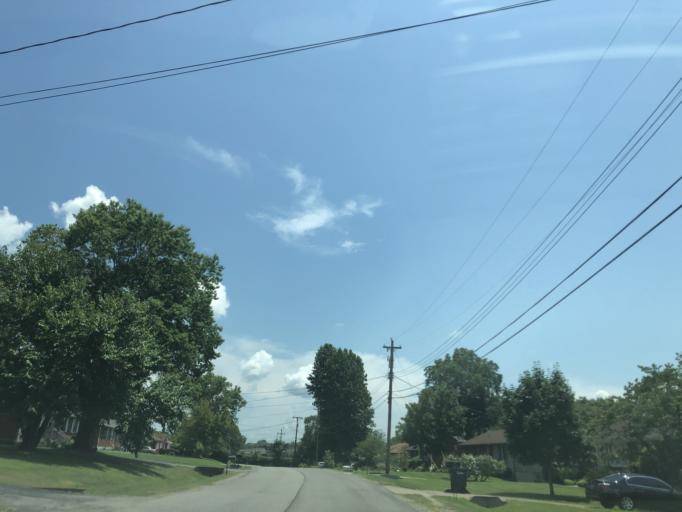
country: US
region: Tennessee
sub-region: Davidson County
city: Lakewood
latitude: 36.1954
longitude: -86.6262
